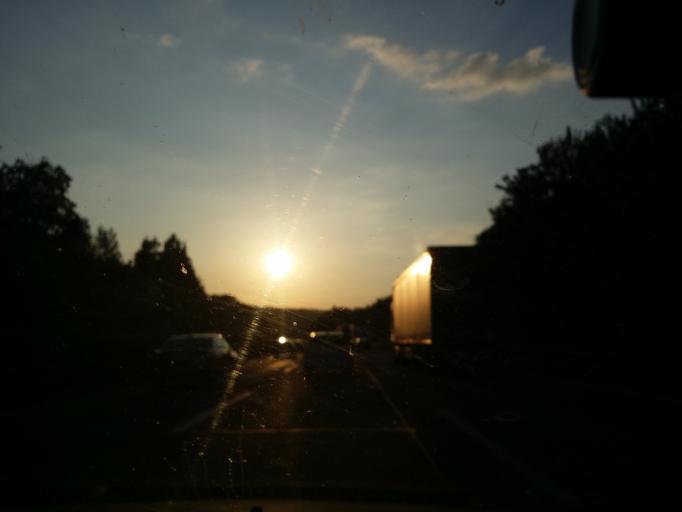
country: DE
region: Hesse
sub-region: Regierungsbezirk Darmstadt
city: Niedernhausen
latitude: 50.1723
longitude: 8.2878
